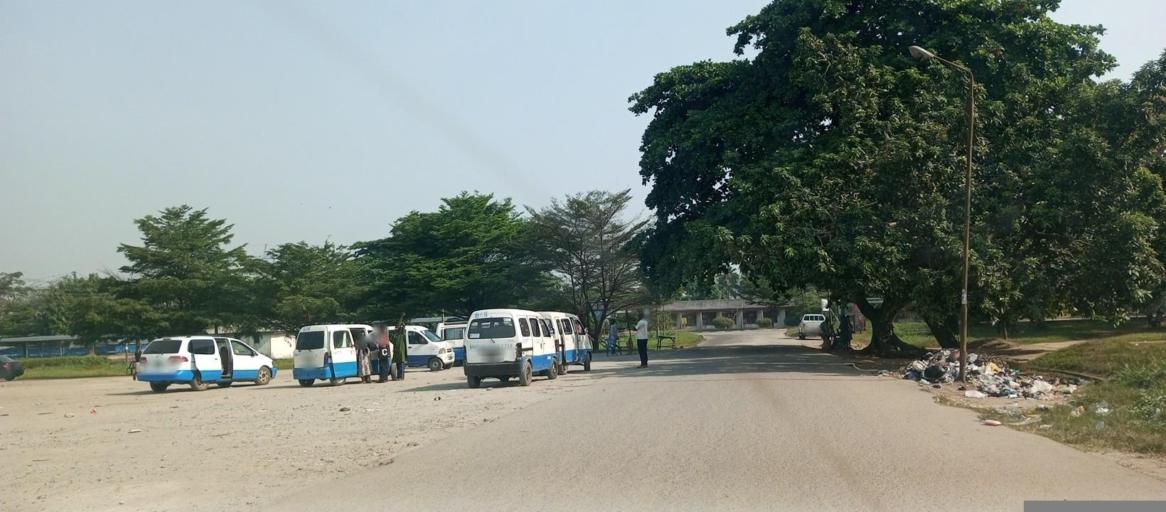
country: NG
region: Rivers
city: Emuoha
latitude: 4.9007
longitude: 6.9223
